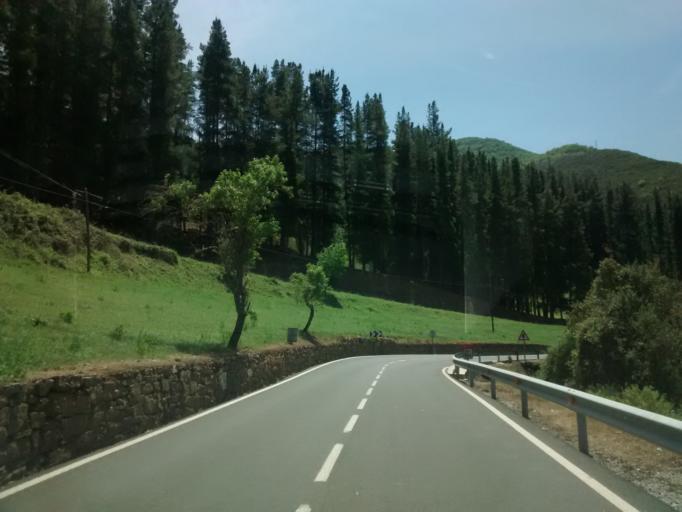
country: ES
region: Cantabria
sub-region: Provincia de Cantabria
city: Potes
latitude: 43.1203
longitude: -4.6287
